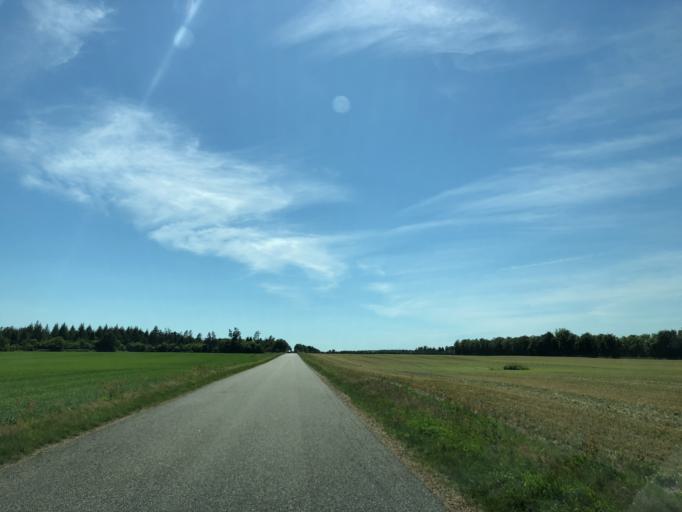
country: DK
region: Central Jutland
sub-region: Skive Kommune
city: Skive
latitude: 56.4434
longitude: 8.9699
